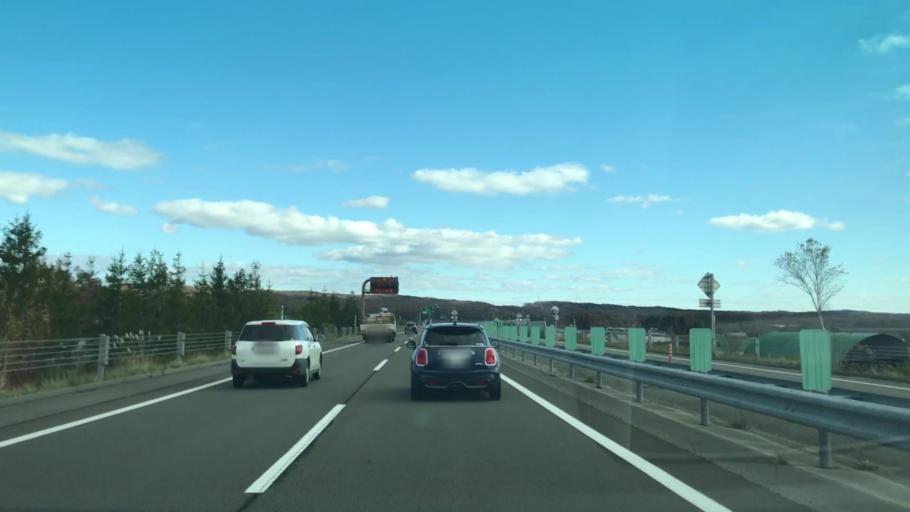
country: JP
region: Hokkaido
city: Chitose
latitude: 42.8836
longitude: 141.7017
